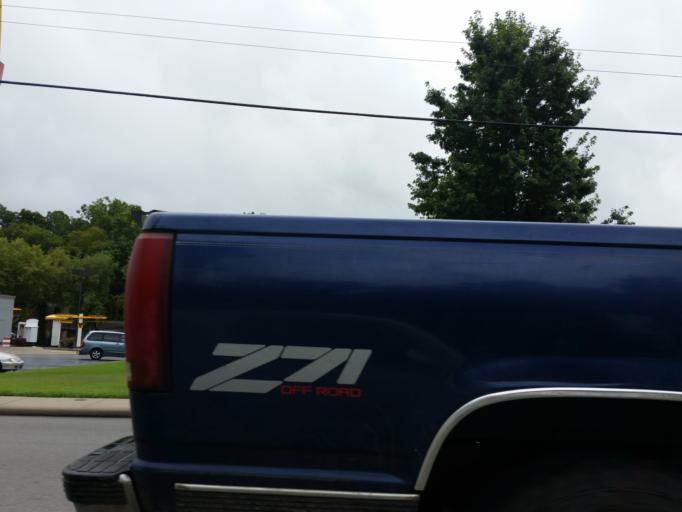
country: US
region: Missouri
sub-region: Cape Girardeau County
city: Cape Girardeau
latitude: 37.3129
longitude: -89.5461
